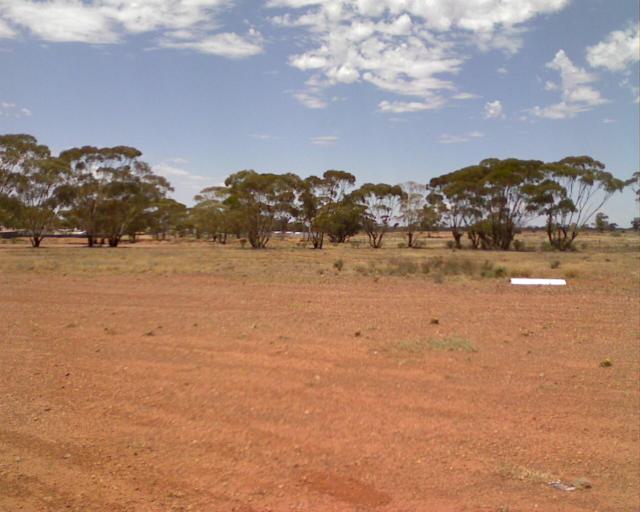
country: AU
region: Western Australia
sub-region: Kalgoorlie/Boulder
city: Boulder
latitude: -30.7819
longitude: 121.4648
